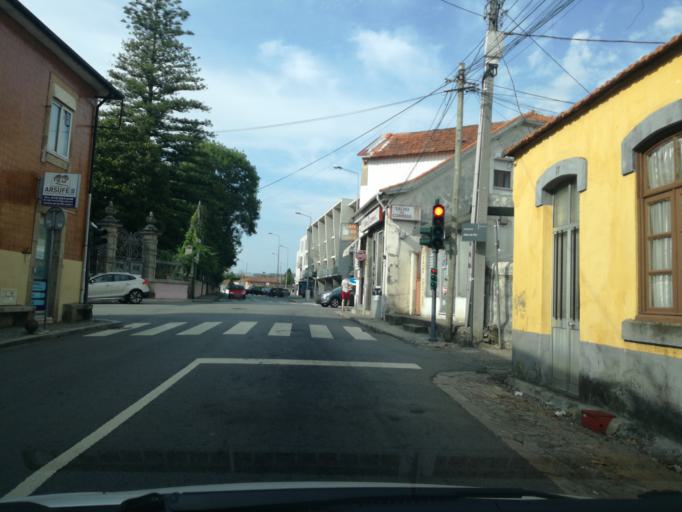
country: PT
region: Porto
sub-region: Vila Nova de Gaia
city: Sao Felix da Marinha
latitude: 41.0423
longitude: -8.6284
